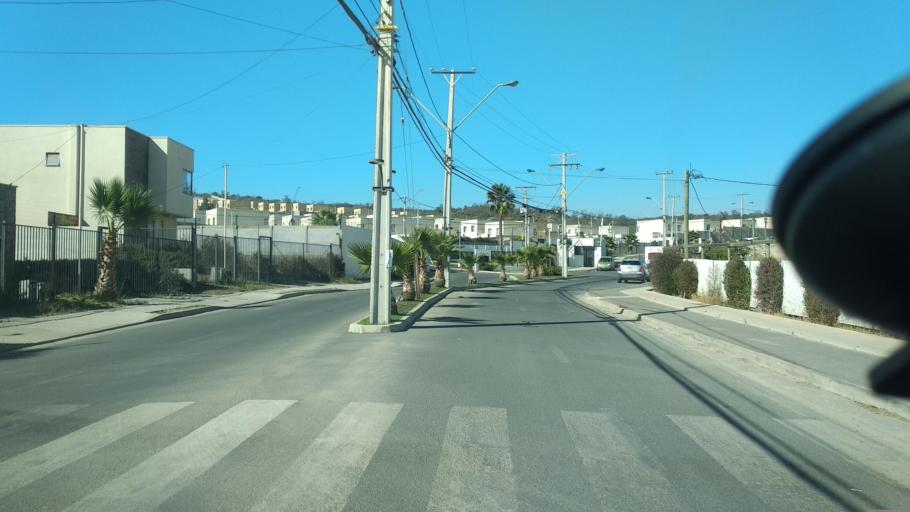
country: CL
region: Valparaiso
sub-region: Provincia de Marga Marga
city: Villa Alemana
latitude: -33.0353
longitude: -71.3875
